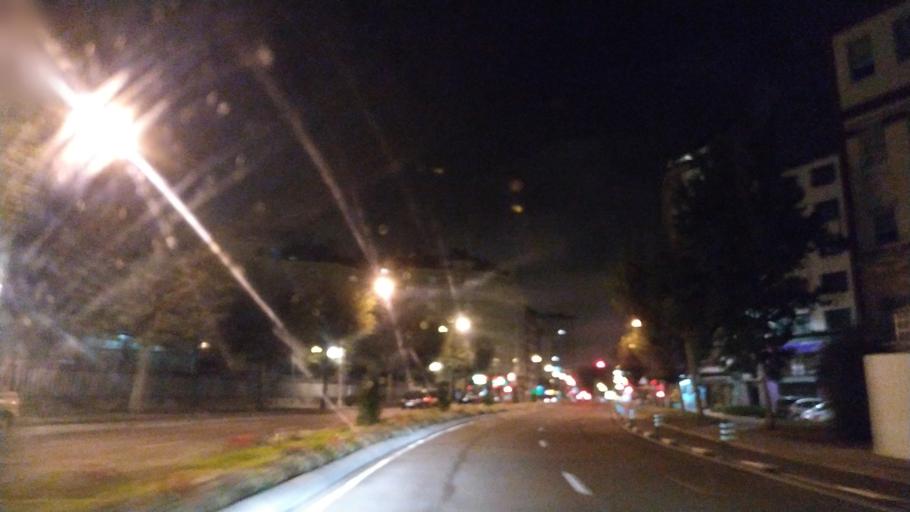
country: ES
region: Galicia
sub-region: Provincia da Coruna
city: A Coruna
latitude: 43.3527
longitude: -8.4031
